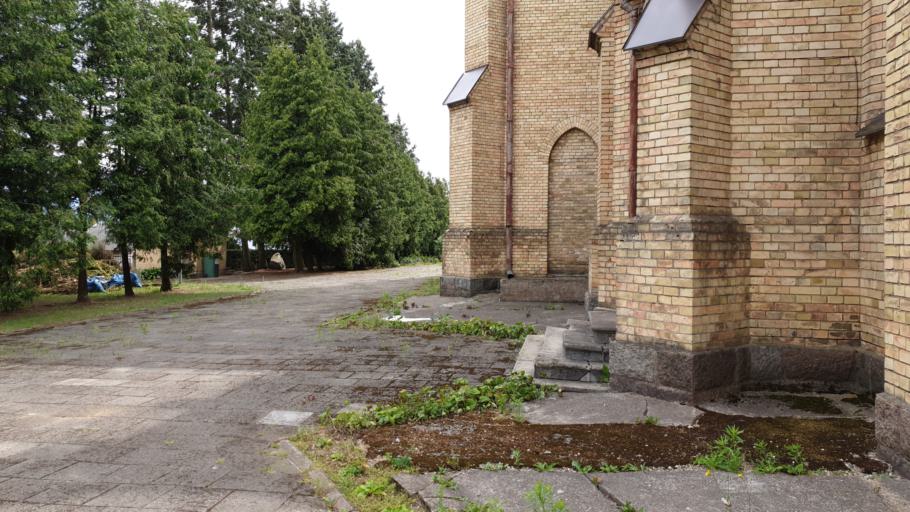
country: LT
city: Skaidiskes
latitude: 54.6976
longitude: 25.4109
